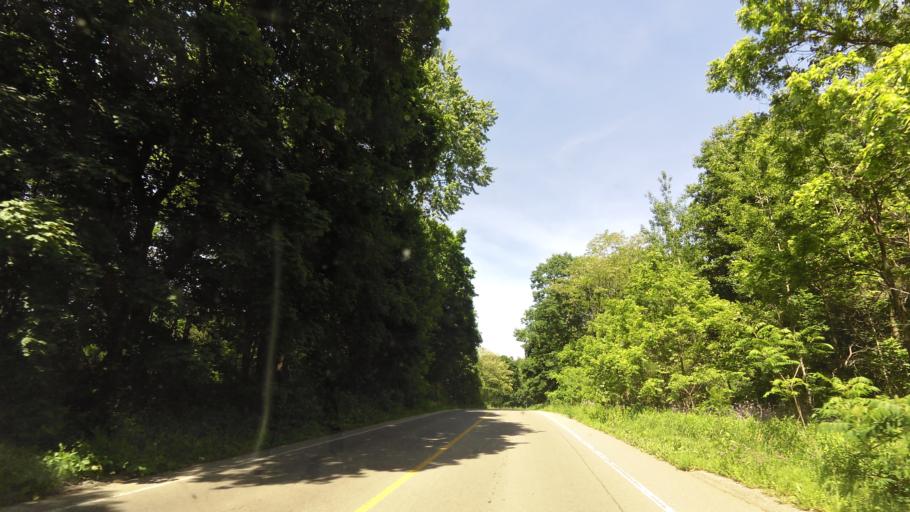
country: CA
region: Ontario
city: Norfolk County
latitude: 42.6970
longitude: -80.3419
